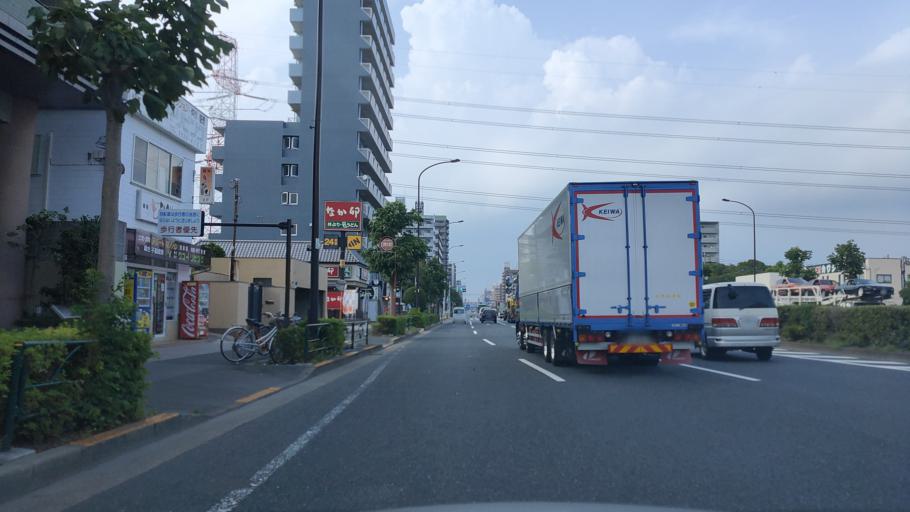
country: JP
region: Tokyo
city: Urayasu
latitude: 35.6490
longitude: 139.8720
